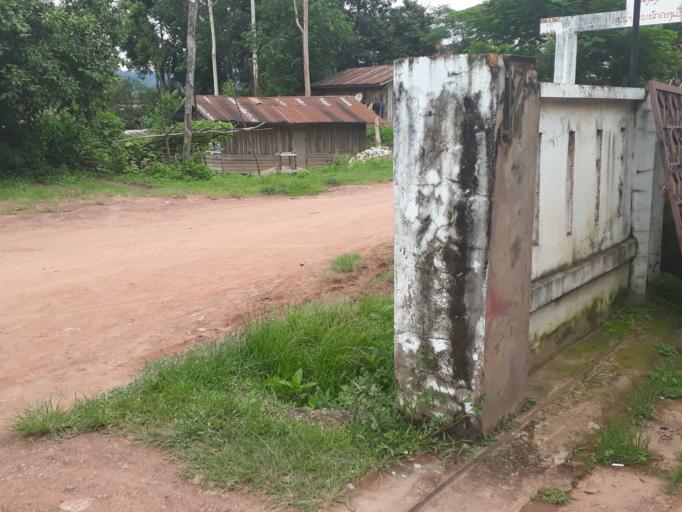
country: LA
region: Phongsali
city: Phongsali
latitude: 21.3867
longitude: 101.9739
